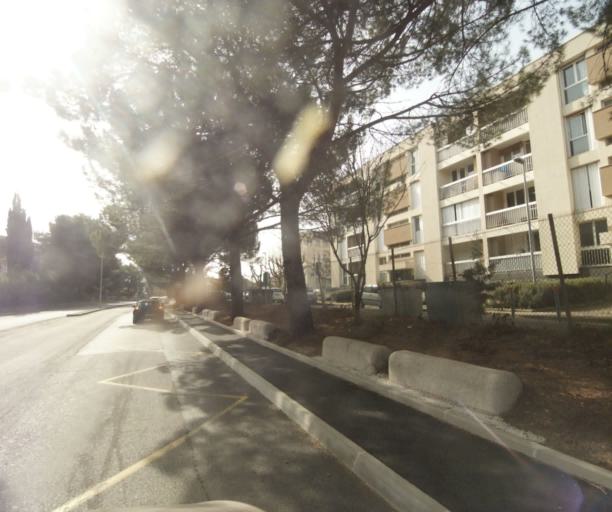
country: FR
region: Provence-Alpes-Cote d'Azur
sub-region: Departement des Bouches-du-Rhone
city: Gardanne
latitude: 43.4554
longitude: 5.4773
